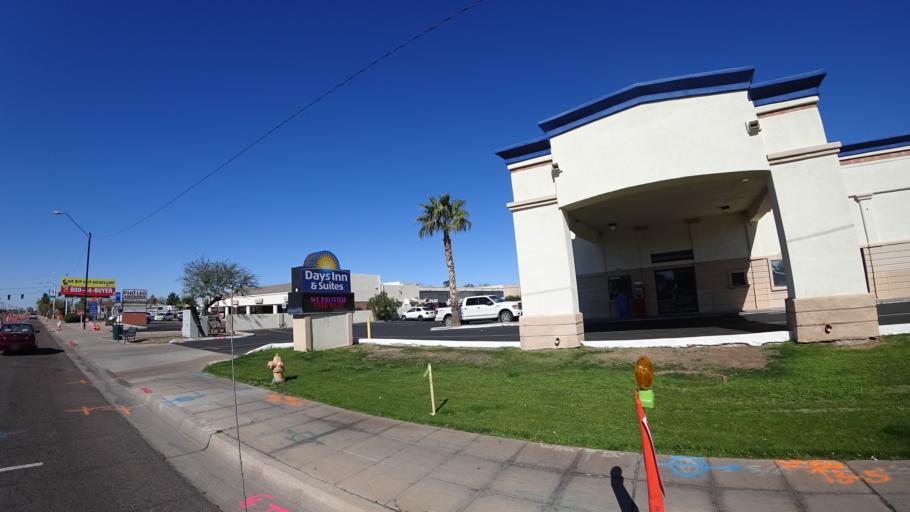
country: US
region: Arizona
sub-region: Maricopa County
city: Mesa
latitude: 33.4155
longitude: -111.7931
